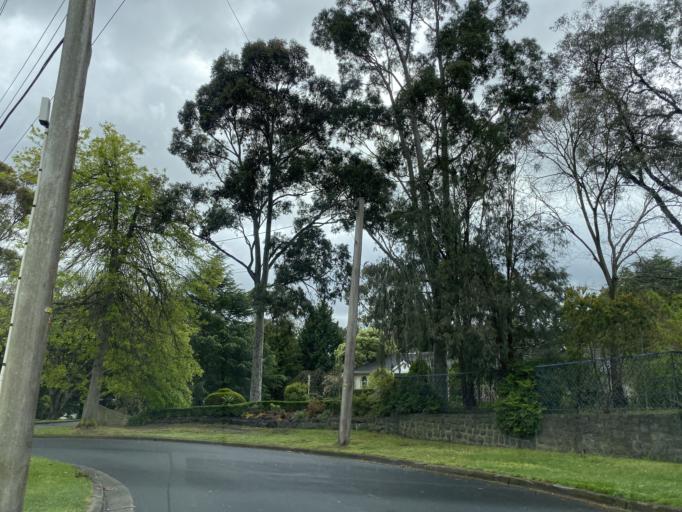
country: AU
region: Victoria
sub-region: Manningham
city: Templestowe Lower
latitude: -37.7652
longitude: 145.1364
